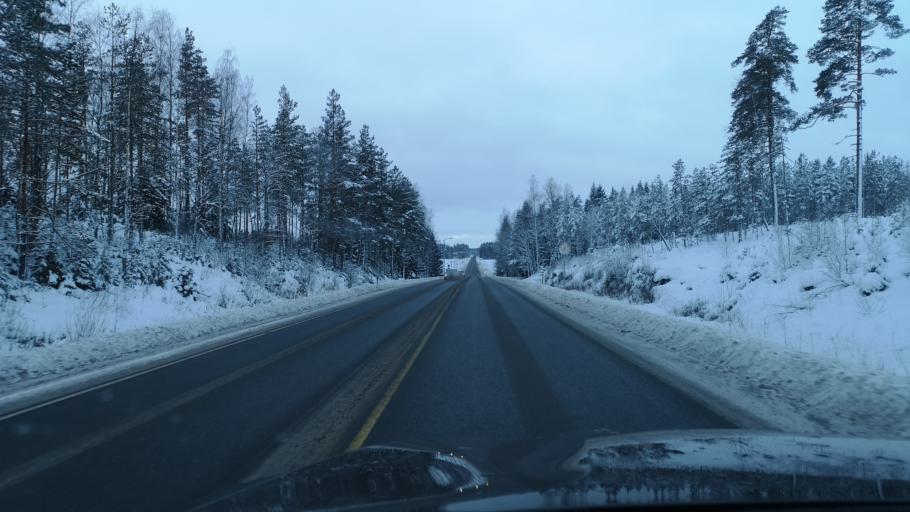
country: FI
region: Haeme
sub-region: Forssa
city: Ypaejae
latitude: 60.9201
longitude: 23.2042
